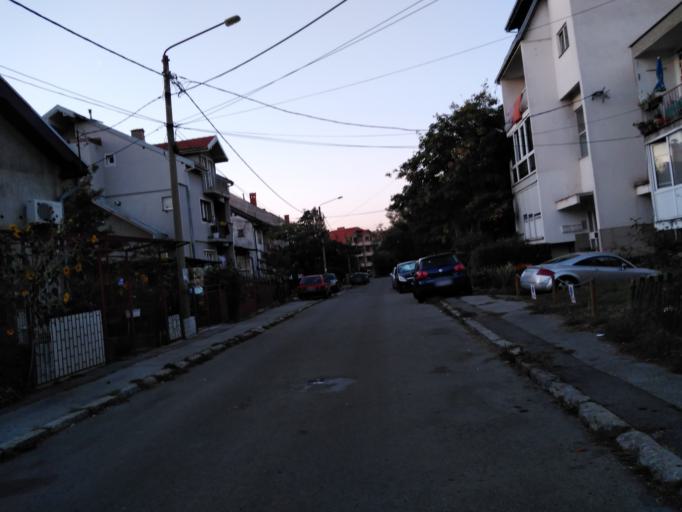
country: RS
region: Central Serbia
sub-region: Belgrade
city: Rakovica
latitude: 44.7511
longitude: 20.4213
